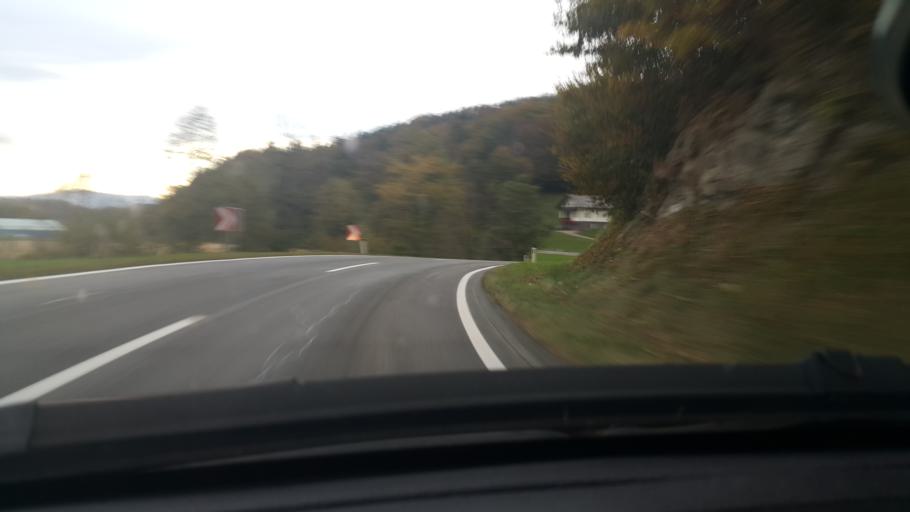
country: AT
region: Styria
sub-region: Politischer Bezirk Leibnitz
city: Arnfels
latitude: 46.6734
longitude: 15.4135
